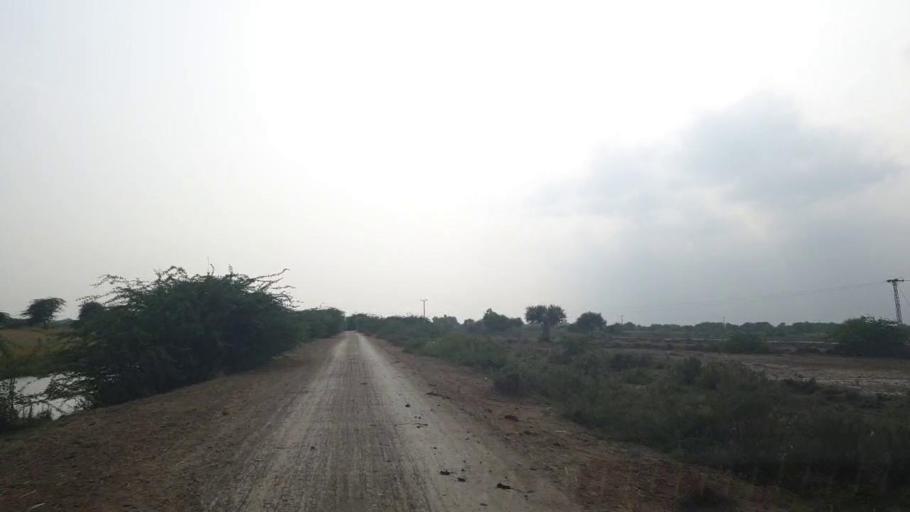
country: PK
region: Sindh
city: Badin
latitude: 24.6245
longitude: 68.6897
